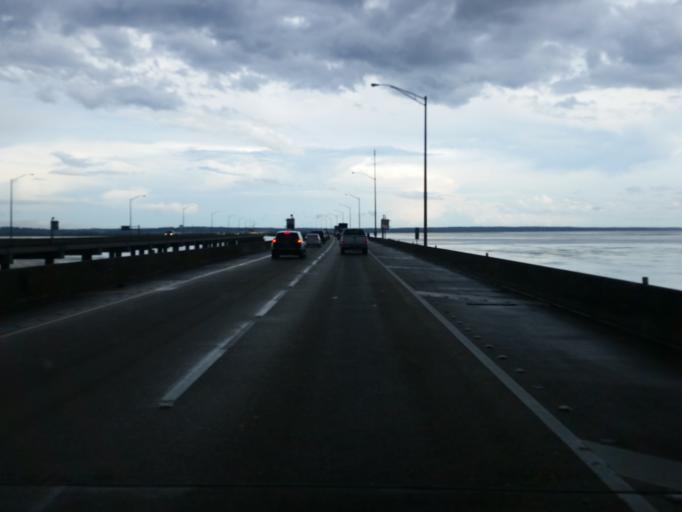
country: US
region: Alabama
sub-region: Baldwin County
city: Spanish Fort
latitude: 30.6721
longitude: -87.9791
